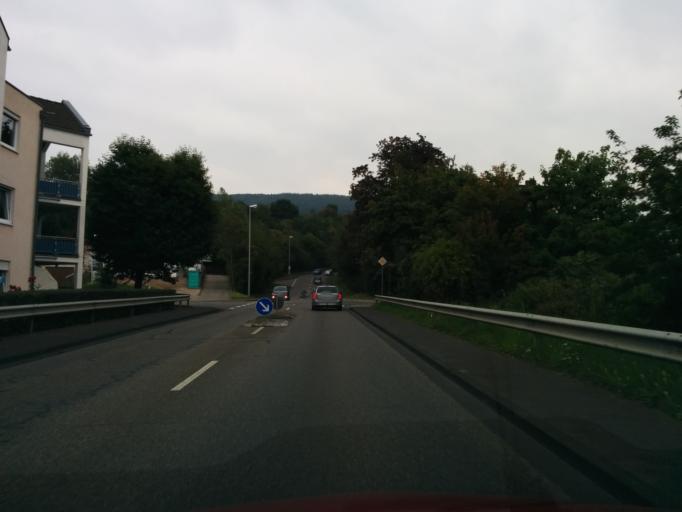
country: DE
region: Rheinland-Pfalz
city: Lahnstein
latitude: 50.3235
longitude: 7.5997
